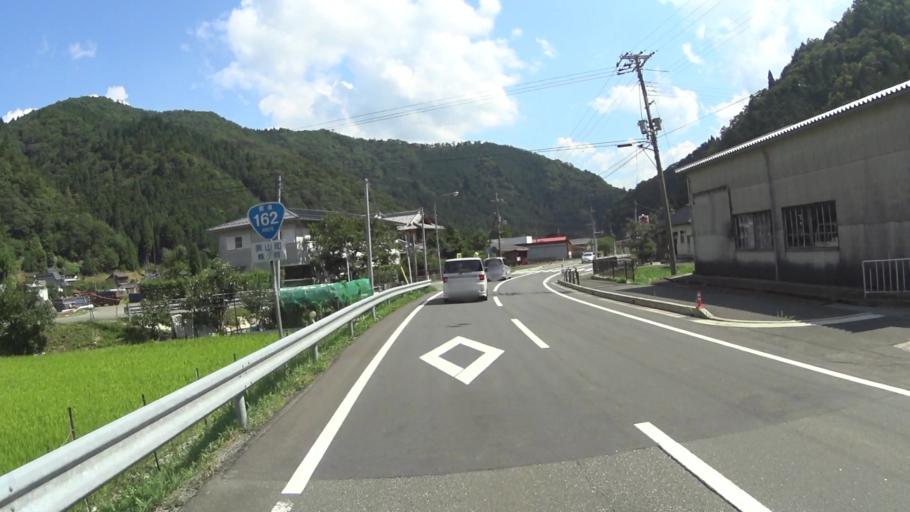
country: JP
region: Kyoto
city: Maizuru
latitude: 35.3200
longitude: 135.5555
